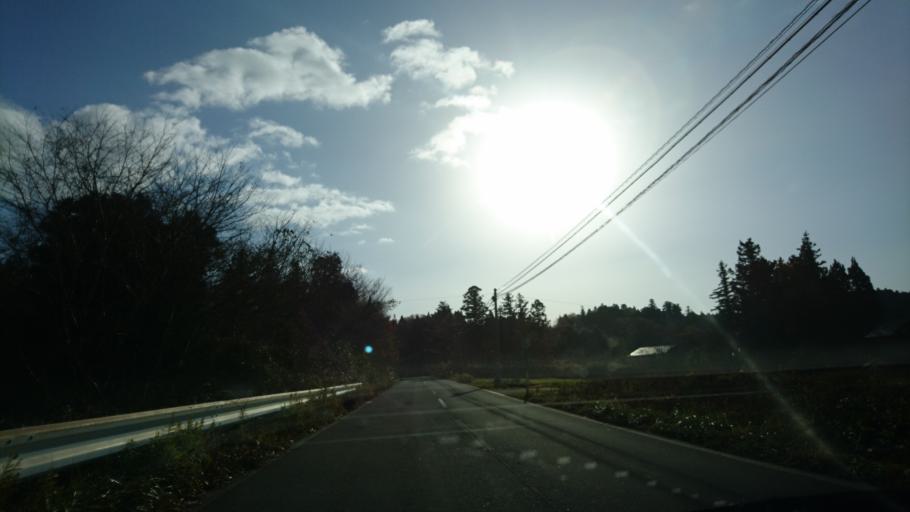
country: JP
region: Iwate
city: Ichinoseki
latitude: 38.8881
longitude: 141.2876
